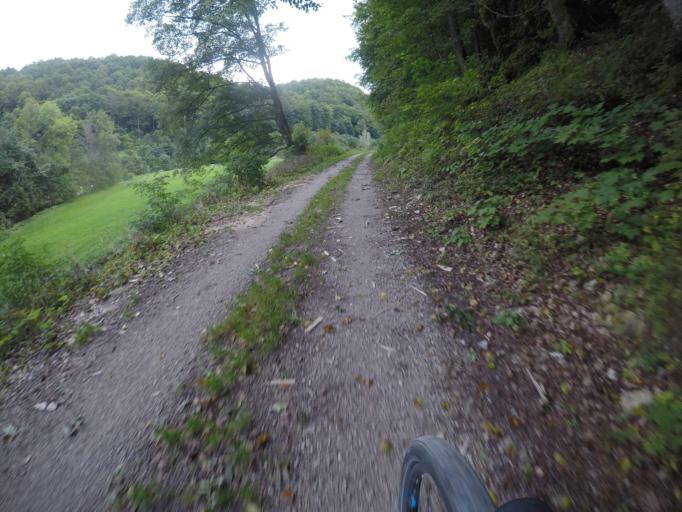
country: DE
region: Baden-Wuerttemberg
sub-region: Tuebingen Region
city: Bad Urach
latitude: 48.4515
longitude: 9.4352
